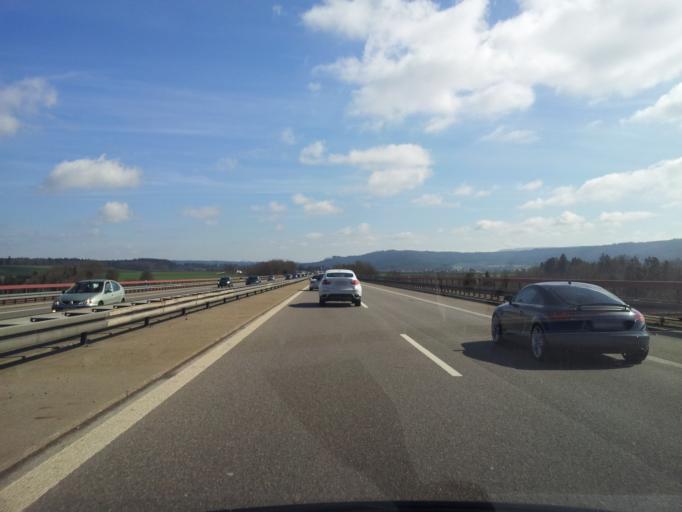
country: DE
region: Baden-Wuerttemberg
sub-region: Freiburg Region
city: Villingendorf
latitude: 48.2018
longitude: 8.6116
